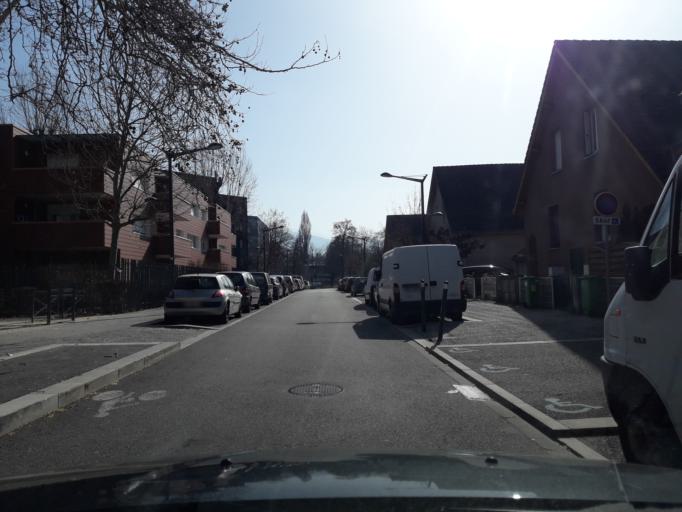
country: FR
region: Rhone-Alpes
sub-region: Departement de l'Isere
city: Grenoble
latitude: 45.1623
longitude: 5.7195
